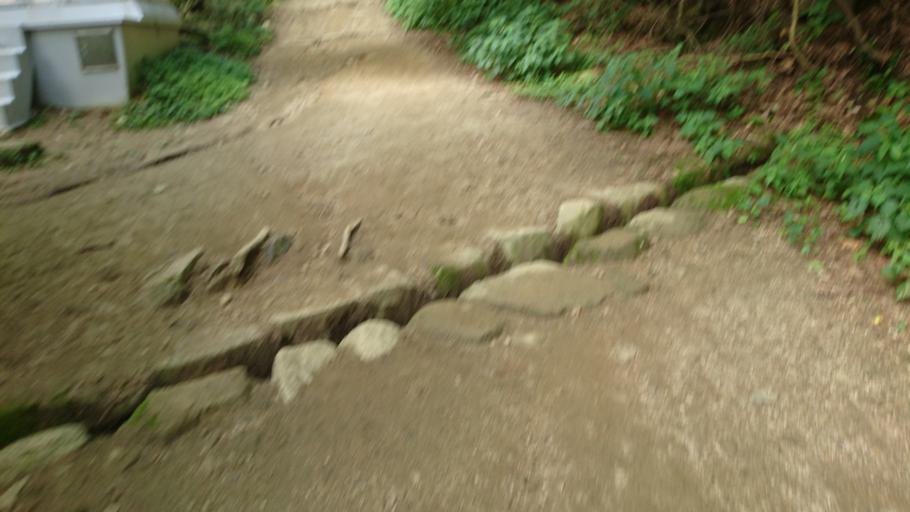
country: KR
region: Daegu
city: Daegu
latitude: 35.9962
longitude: 128.6827
